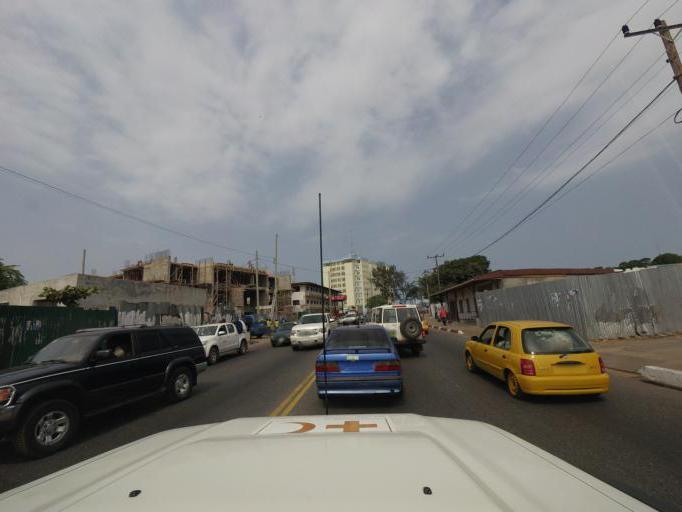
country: LR
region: Montserrado
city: Monrovia
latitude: 6.2946
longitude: -10.7922
